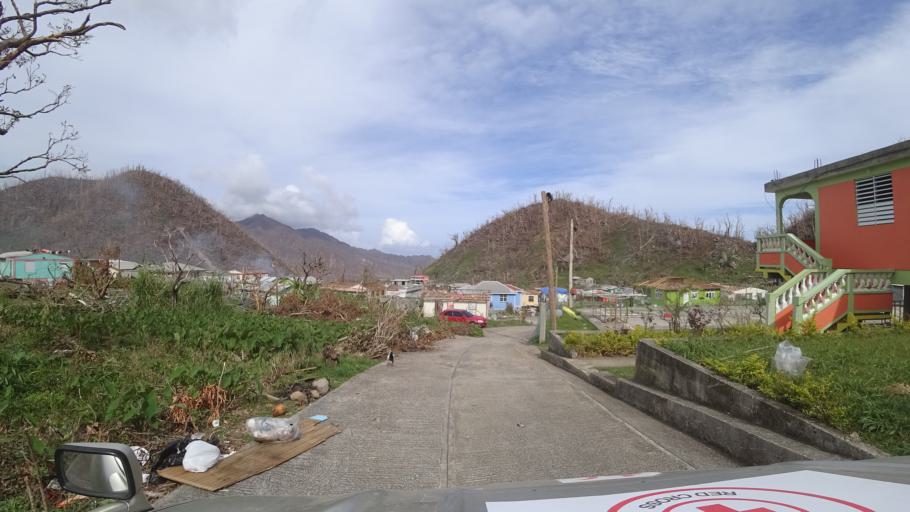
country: DM
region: Saint Patrick
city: Berekua
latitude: 15.2349
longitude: -61.3337
